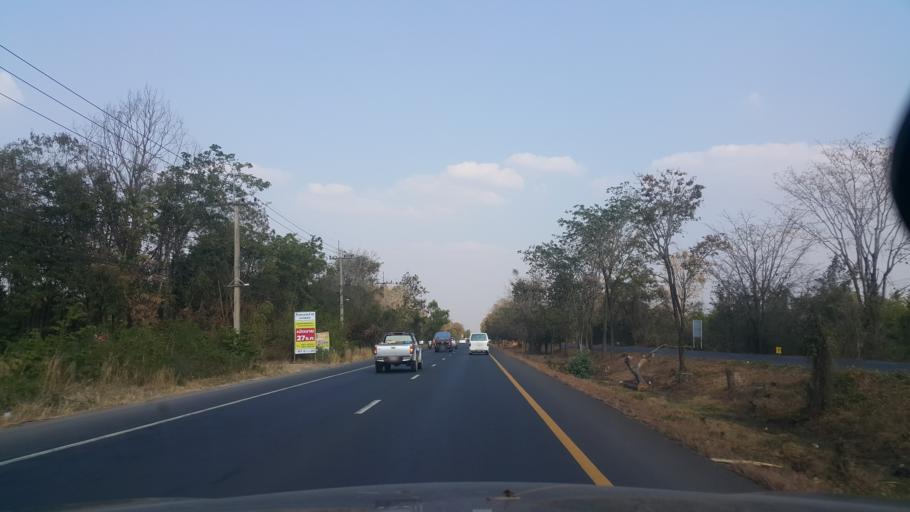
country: TH
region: Buriram
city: Nang Rong
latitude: 14.6333
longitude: 102.7258
